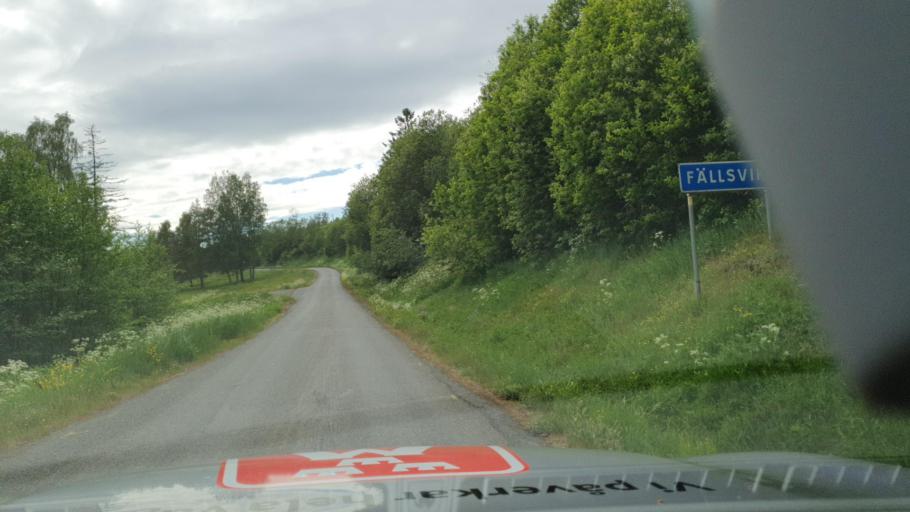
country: SE
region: Vaesternorrland
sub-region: Kramfors Kommun
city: Nordingra
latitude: 62.8491
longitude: 18.3415
